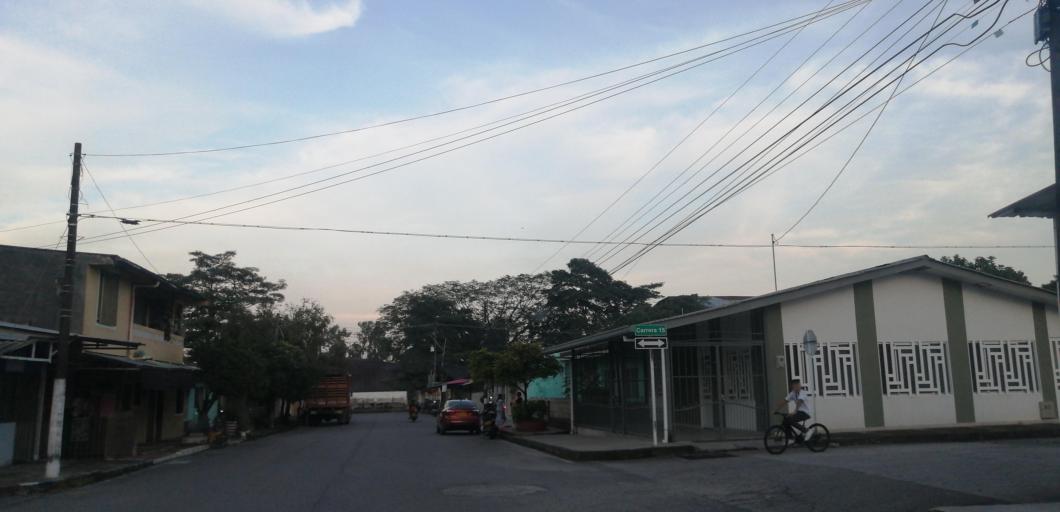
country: CO
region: Meta
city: Acacias
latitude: 3.9917
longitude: -73.7579
